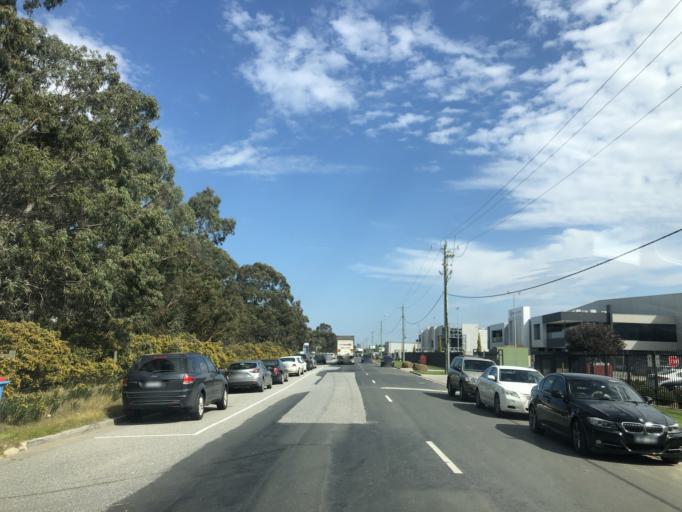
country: AU
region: Victoria
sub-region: Casey
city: Hampton Park
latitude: -38.0352
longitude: 145.2287
